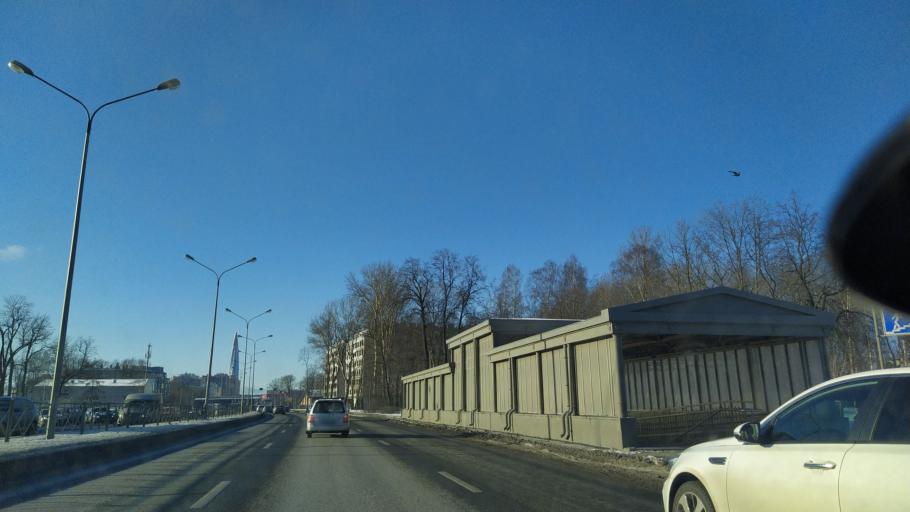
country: RU
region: St.-Petersburg
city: Staraya Derevnya
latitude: 59.9832
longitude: 30.2541
